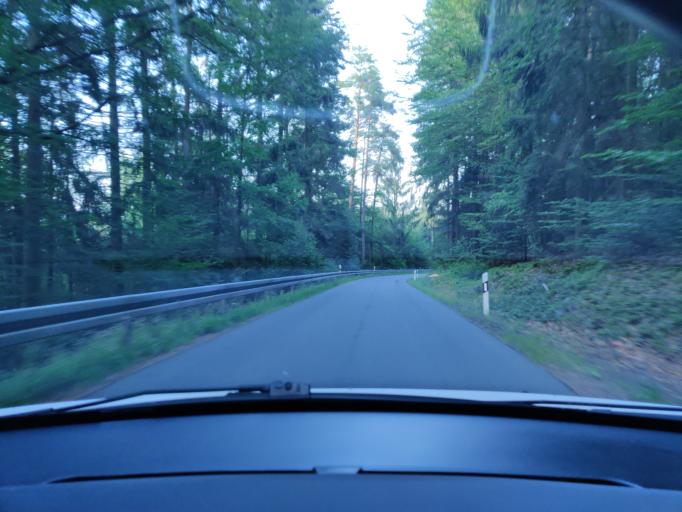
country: DE
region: Bavaria
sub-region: Upper Palatinate
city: Nabburg
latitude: 49.4277
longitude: 12.1794
